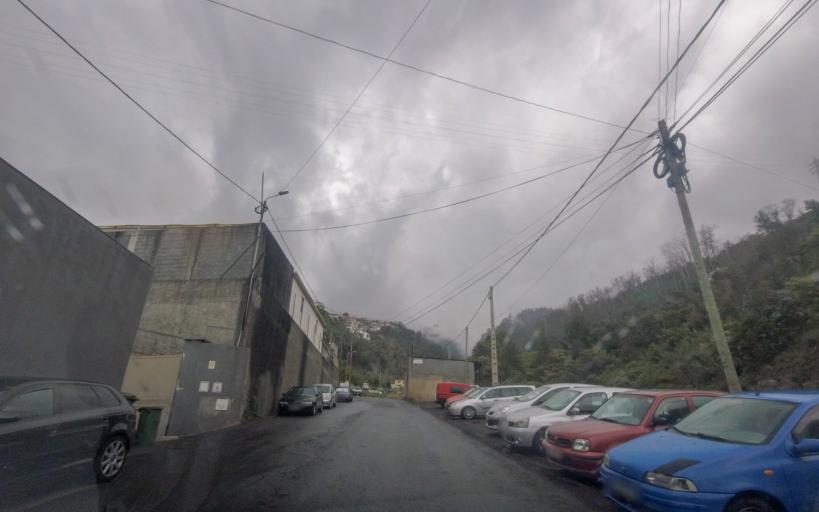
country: PT
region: Madeira
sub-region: Funchal
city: Nossa Senhora do Monte
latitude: 32.6729
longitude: -16.9349
